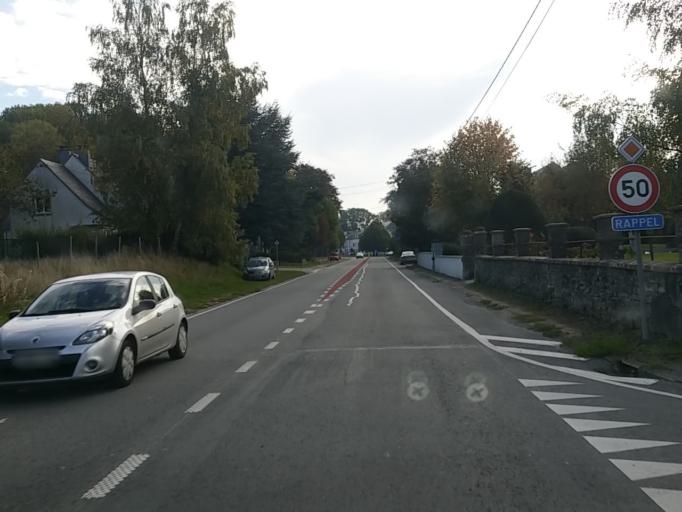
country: BE
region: Wallonia
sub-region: Province du Luxembourg
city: Florenville
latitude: 49.6975
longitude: 5.3008
